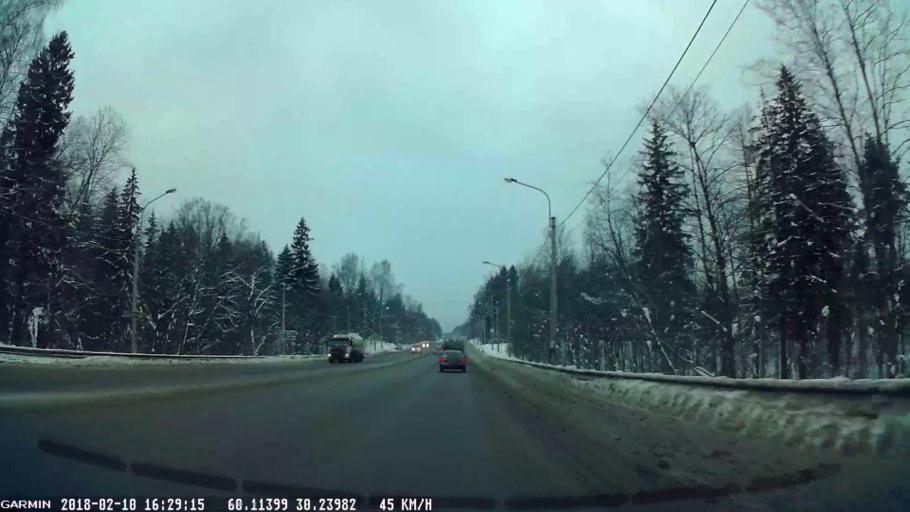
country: RU
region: St.-Petersburg
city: Levashovo
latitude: 60.1144
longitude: 30.2393
